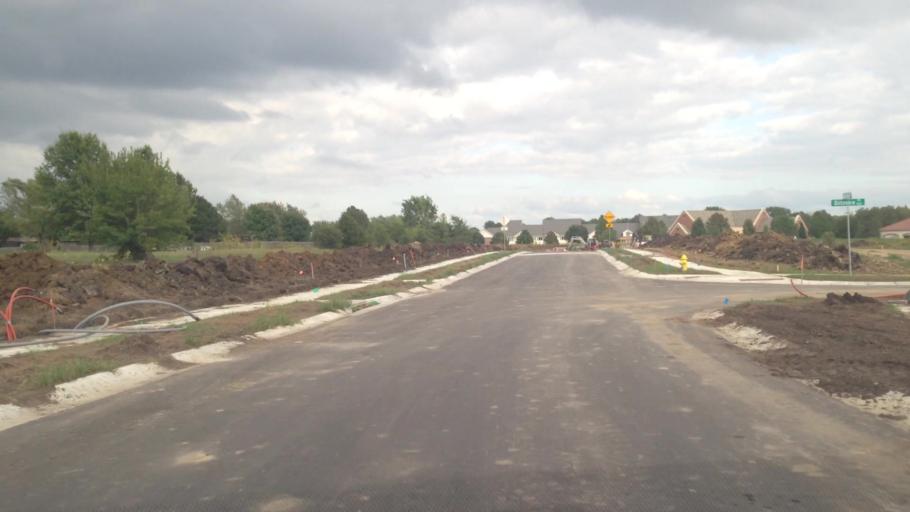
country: US
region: Kansas
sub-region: Douglas County
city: Lawrence
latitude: 38.9660
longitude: -95.3113
